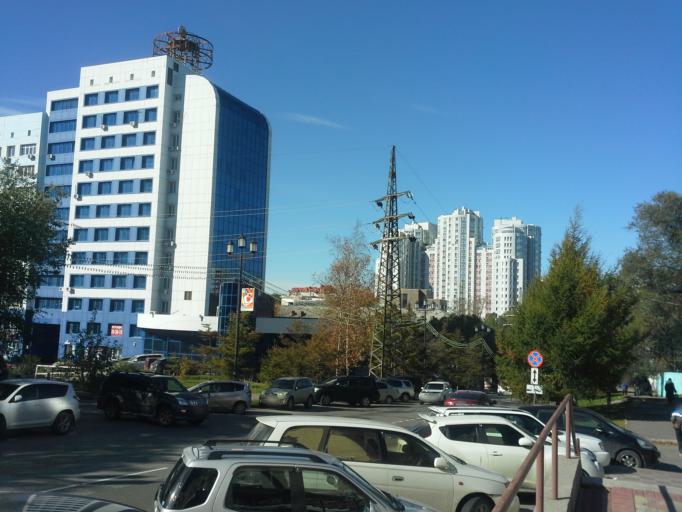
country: RU
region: Khabarovsk Krai
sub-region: Khabarovskiy Rayon
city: Khabarovsk
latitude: 48.4689
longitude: 135.0629
